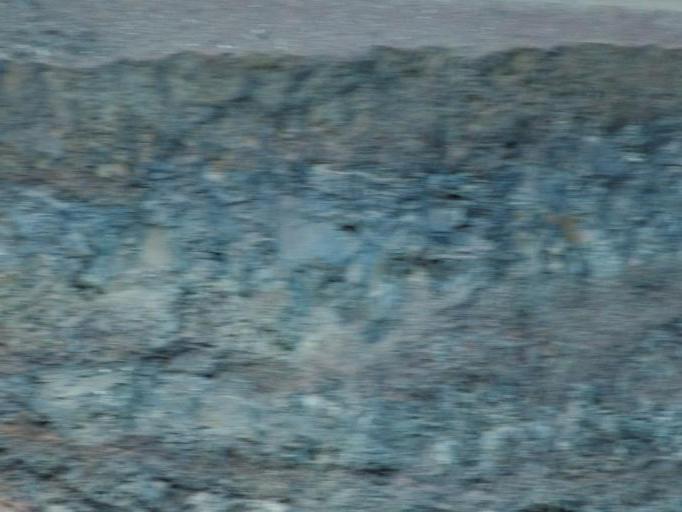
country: ES
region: Canary Islands
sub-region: Provincia de Santa Cruz de Tenerife
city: San Sebastian de la Gomera
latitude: 28.0875
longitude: -17.1267
